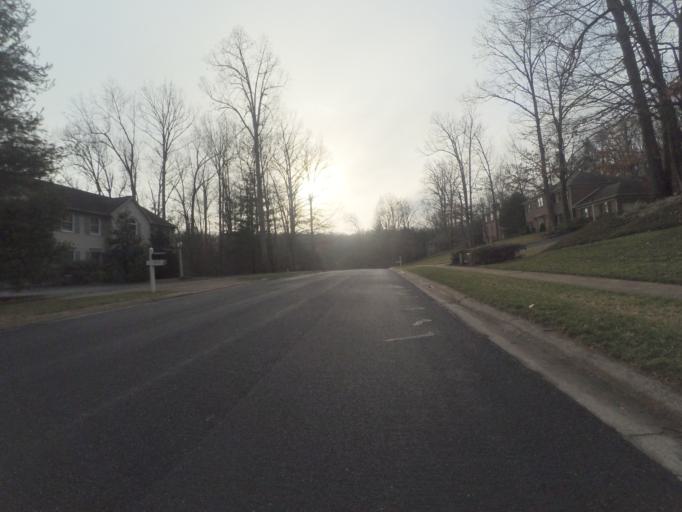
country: US
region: Pennsylvania
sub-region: Centre County
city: Park Forest Village
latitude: 40.7901
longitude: -77.9157
